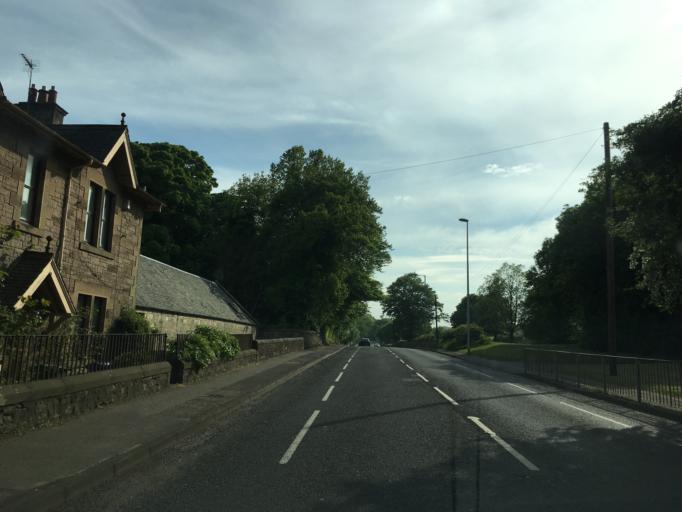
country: GB
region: Scotland
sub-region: Midlothian
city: Penicuik
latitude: 55.8424
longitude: -3.2101
